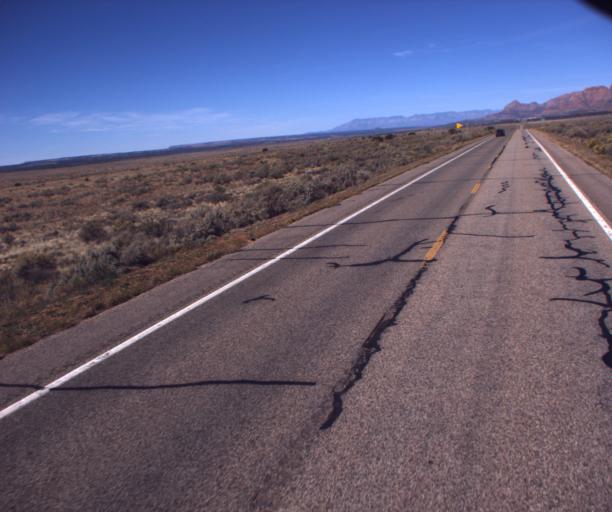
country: US
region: Arizona
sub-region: Mohave County
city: Colorado City
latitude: 36.9008
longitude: -112.9195
